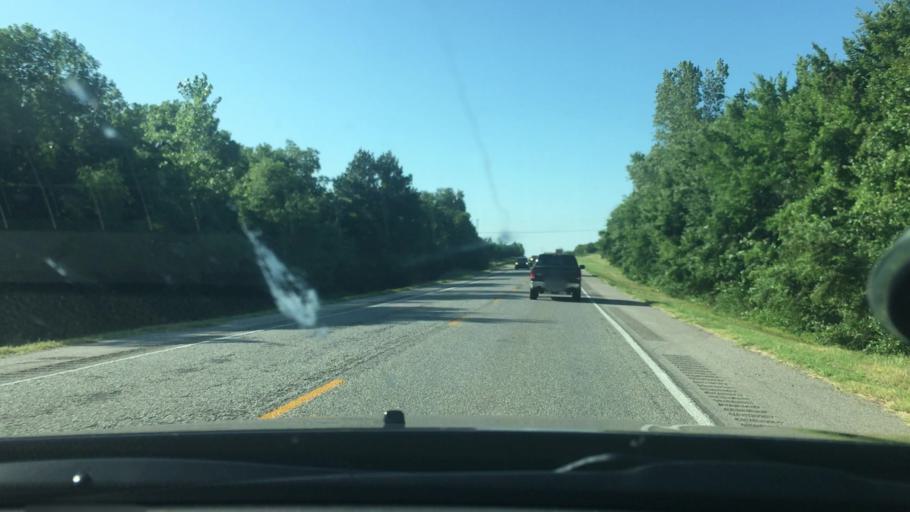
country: US
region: Oklahoma
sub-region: Johnston County
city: Tishomingo
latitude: 34.2686
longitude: -96.7735
